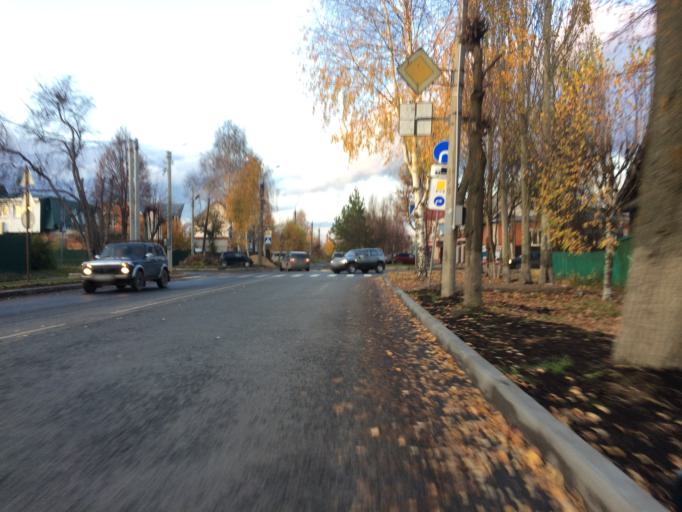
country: RU
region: Mariy-El
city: Yoshkar-Ola
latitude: 56.6522
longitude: 47.8962
